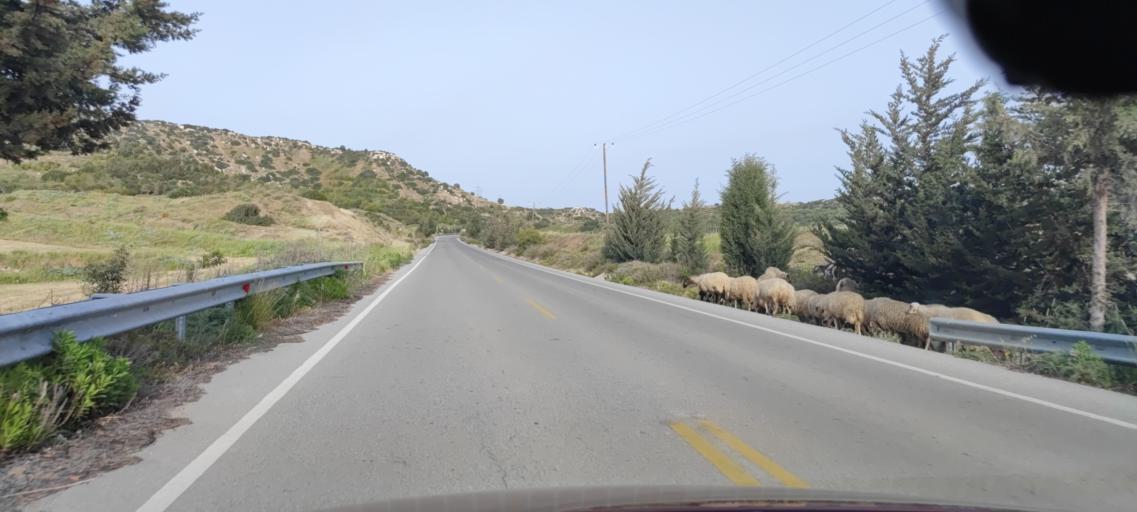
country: CY
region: Ammochostos
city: Leonarisso
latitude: 35.4774
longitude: 34.1300
